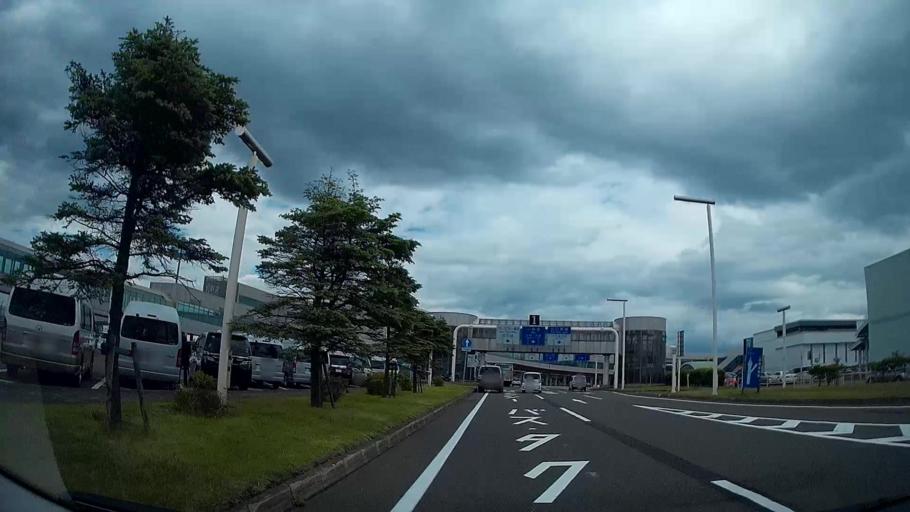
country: JP
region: Hokkaido
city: Chitose
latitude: 42.7892
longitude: 141.6778
